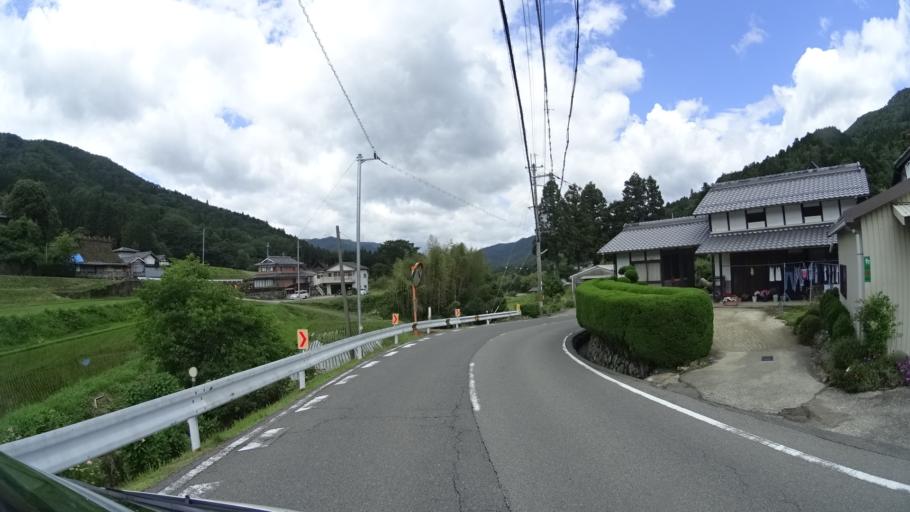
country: JP
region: Kyoto
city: Kameoka
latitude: 35.0117
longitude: 135.4482
